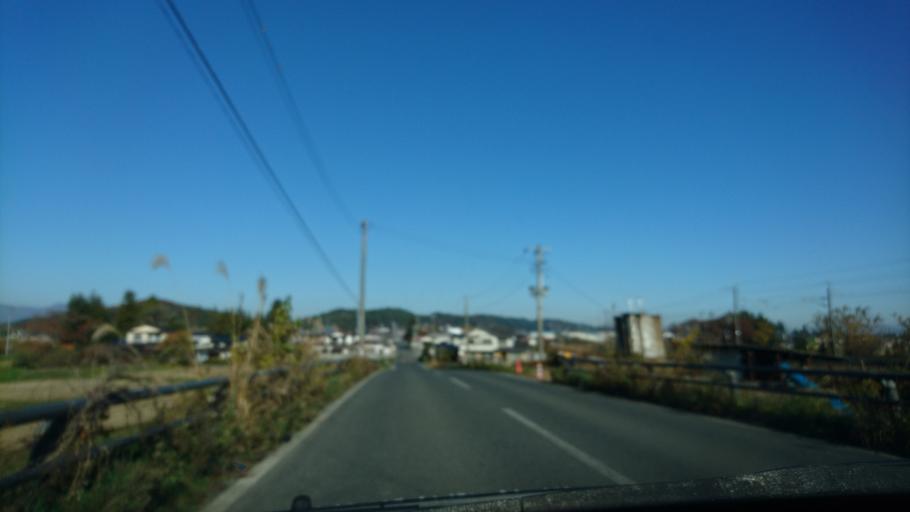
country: JP
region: Iwate
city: Mizusawa
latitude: 39.0330
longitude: 141.1256
